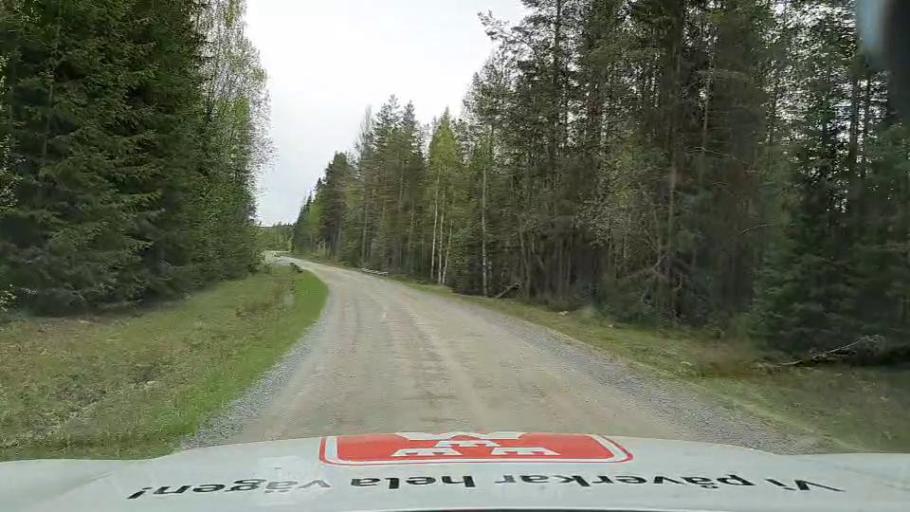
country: SE
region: Jaemtland
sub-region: Bergs Kommun
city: Hoverberg
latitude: 62.5068
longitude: 14.6996
